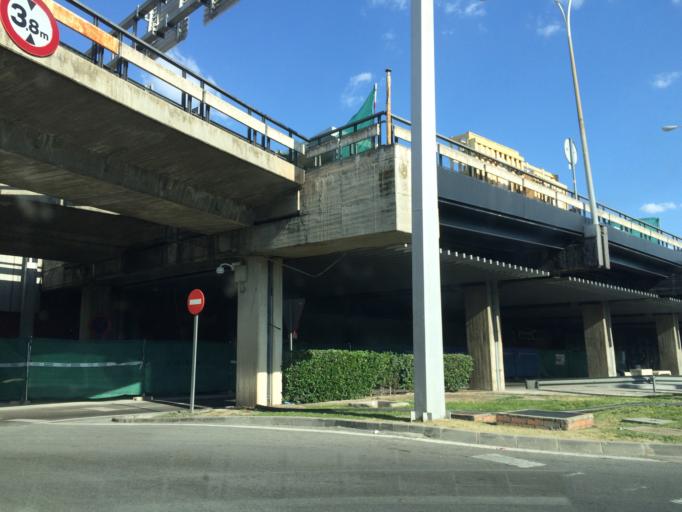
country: ES
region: Madrid
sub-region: Provincia de Madrid
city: Barajas de Madrid
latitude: 40.4657
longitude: -3.5706
